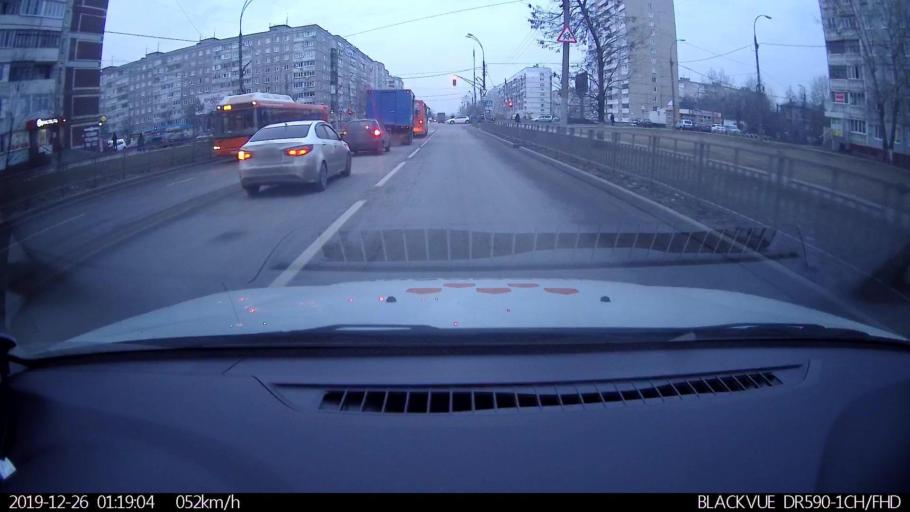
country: RU
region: Nizjnij Novgorod
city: Nizhniy Novgorod
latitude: 56.2703
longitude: 43.8904
